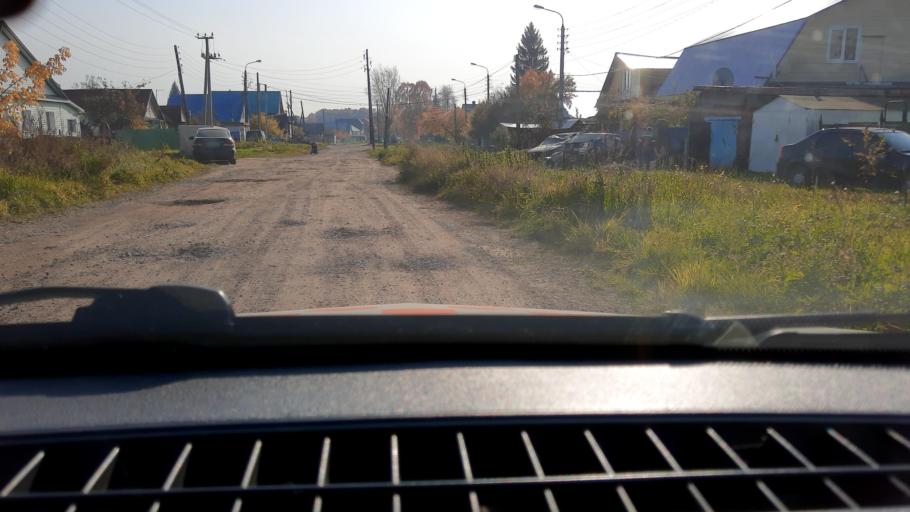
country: RU
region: Bashkortostan
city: Ufa
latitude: 54.8443
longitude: 56.1555
